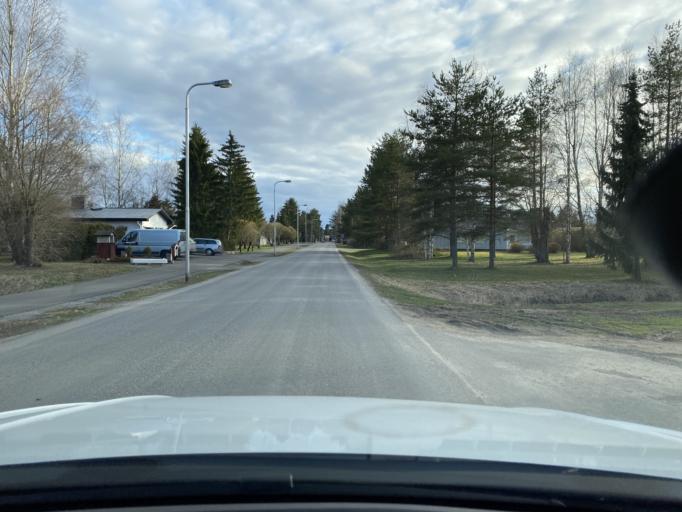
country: FI
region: Pirkanmaa
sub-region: Lounais-Pirkanmaa
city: Punkalaidun
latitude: 61.1164
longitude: 23.1110
